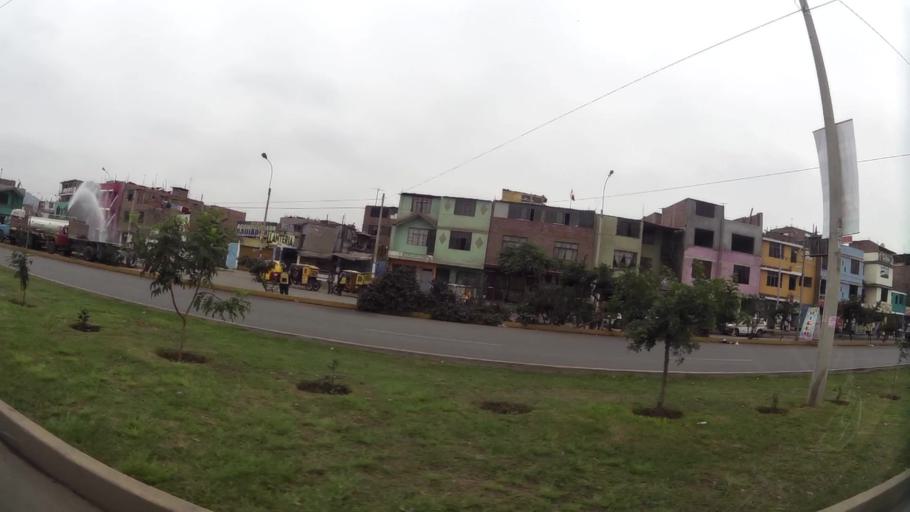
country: PE
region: Lima
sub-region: Lima
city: Vitarte
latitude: -12.0336
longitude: -76.9263
